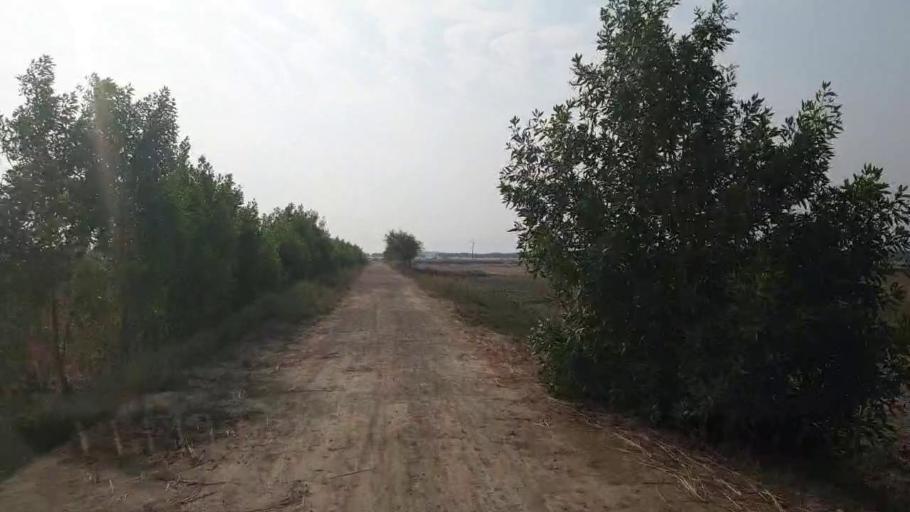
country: PK
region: Sindh
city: Tando Muhammad Khan
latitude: 25.0969
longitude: 68.5076
